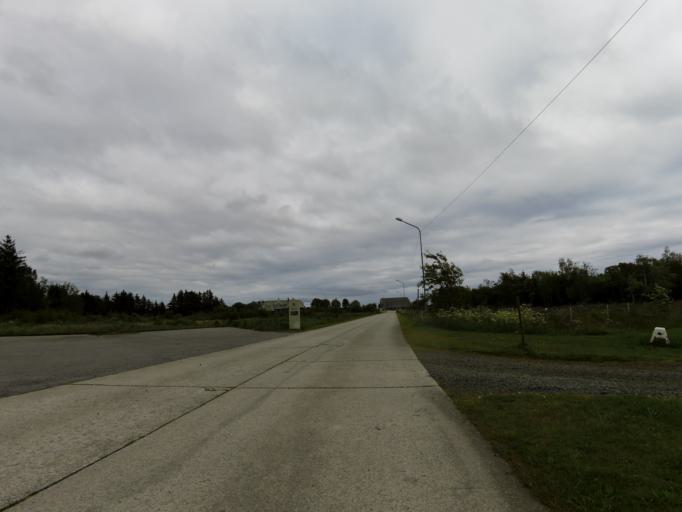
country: NO
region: Vest-Agder
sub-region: Farsund
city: Vestbygd
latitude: 58.1161
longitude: 6.6117
